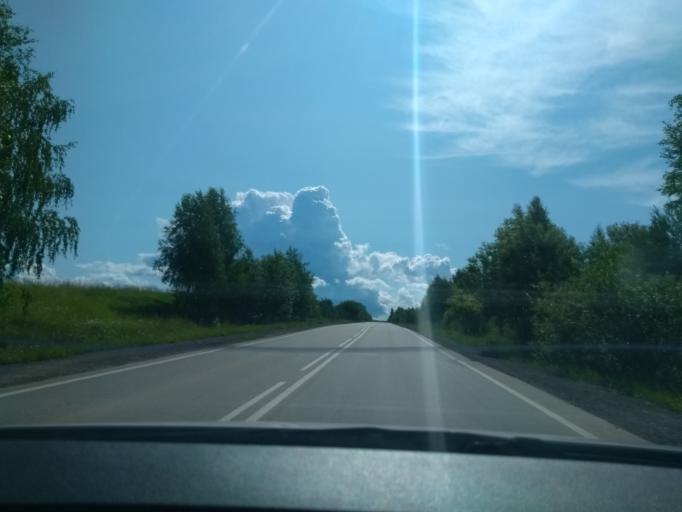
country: RU
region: Perm
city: Bershet'
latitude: 57.8156
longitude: 56.4468
